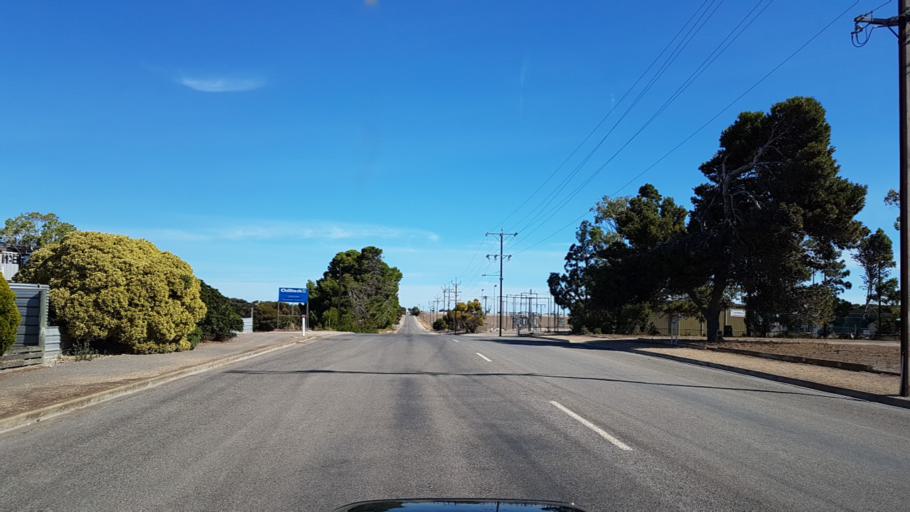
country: AU
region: South Australia
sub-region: Yorke Peninsula
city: Honiton
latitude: -34.9916
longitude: 137.4011
